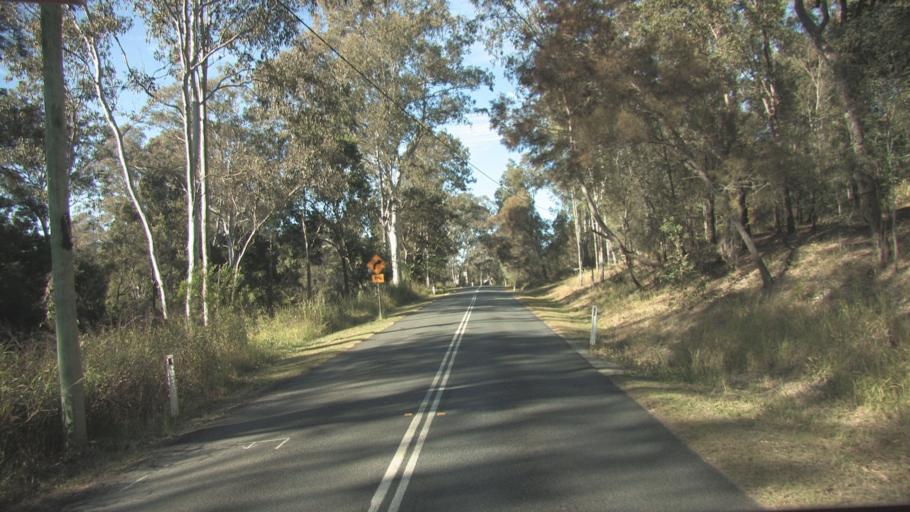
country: AU
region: Queensland
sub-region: Logan
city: Windaroo
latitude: -27.8054
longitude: 153.1696
